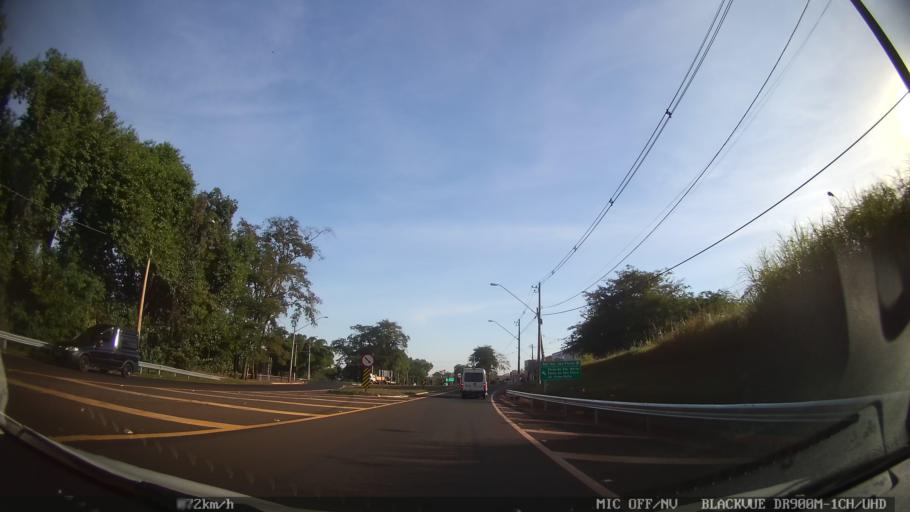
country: BR
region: Sao Paulo
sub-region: Ribeirao Preto
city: Ribeirao Preto
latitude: -21.2787
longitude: -47.8161
